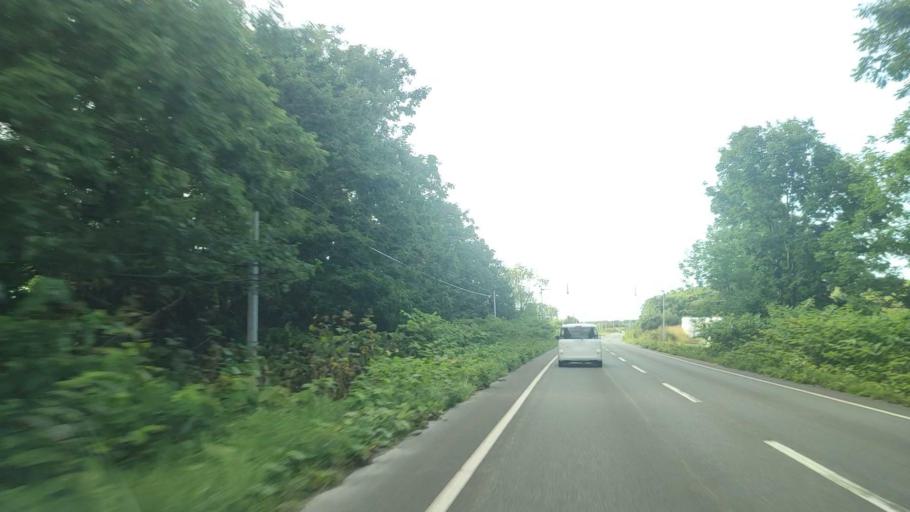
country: JP
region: Hokkaido
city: Makubetsu
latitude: 45.0530
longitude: 141.7500
